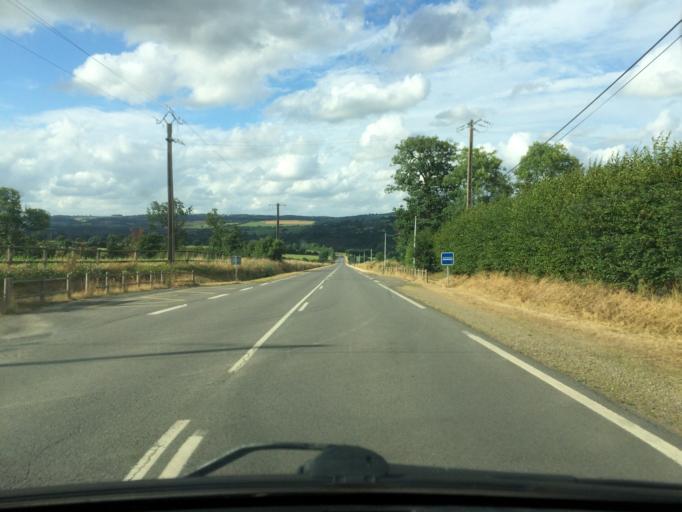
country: FR
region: Lower Normandy
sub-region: Departement du Calvados
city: Clecy
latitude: 48.8605
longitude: -0.4094
